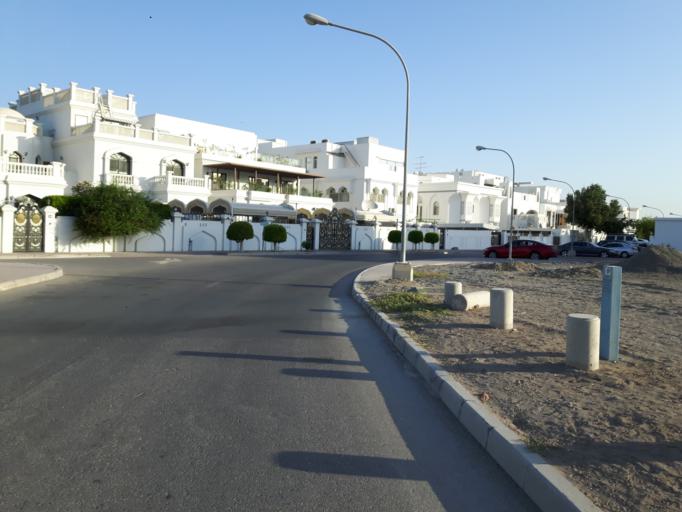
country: OM
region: Muhafazat Masqat
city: Bawshar
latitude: 23.6092
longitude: 58.4488
